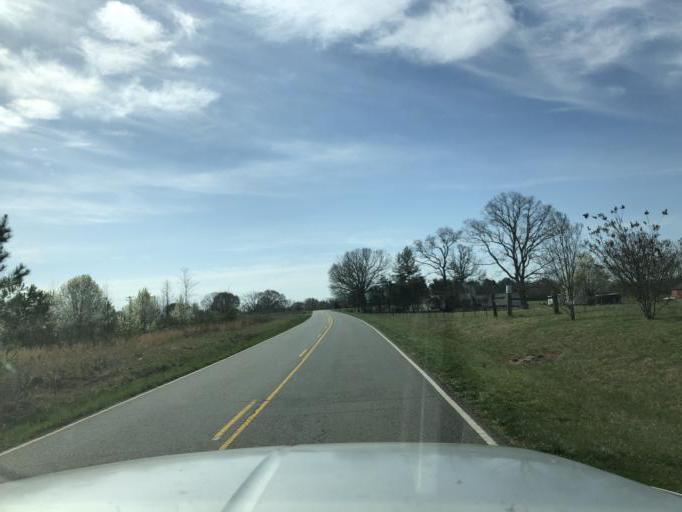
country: US
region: North Carolina
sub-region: Cleveland County
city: Shelby
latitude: 35.3917
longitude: -81.6247
